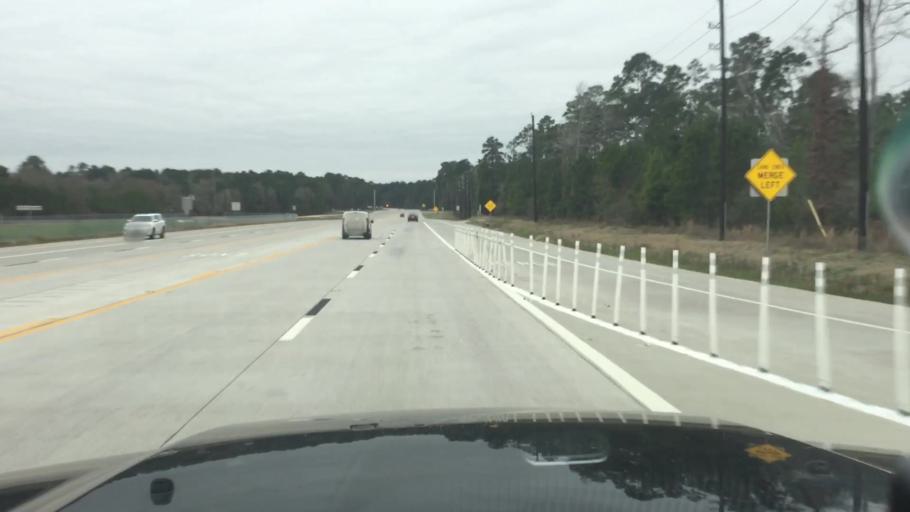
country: US
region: Texas
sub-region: Montgomery County
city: Magnolia
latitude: 30.2292
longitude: -95.6989
